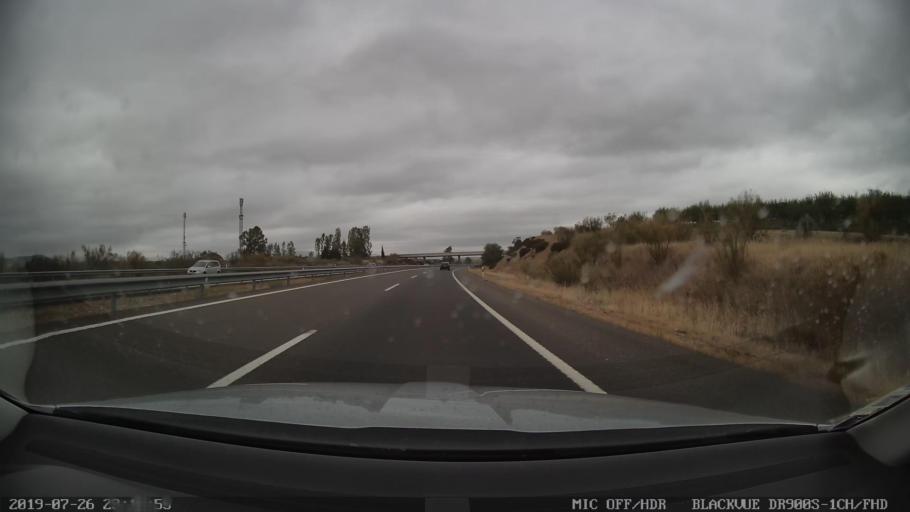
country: ES
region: Extremadura
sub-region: Provincia de Badajoz
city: Santa Amalia
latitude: 39.0619
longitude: -6.0551
